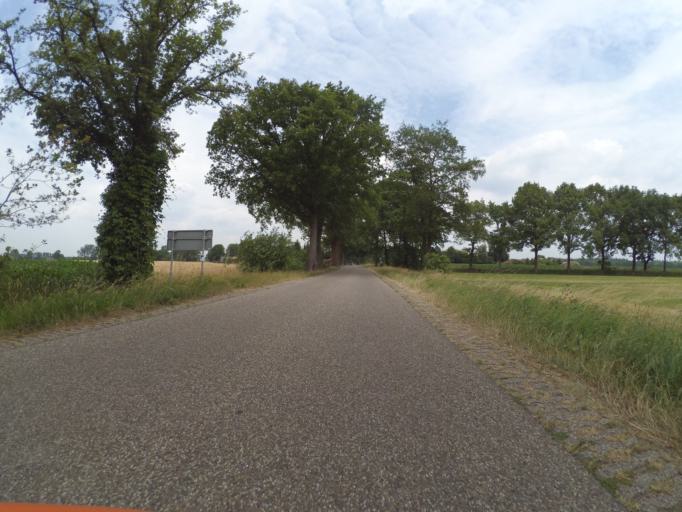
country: NL
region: Overijssel
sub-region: Gemeente Hof van Twente
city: Diepenheim
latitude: 52.1792
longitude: 6.5145
